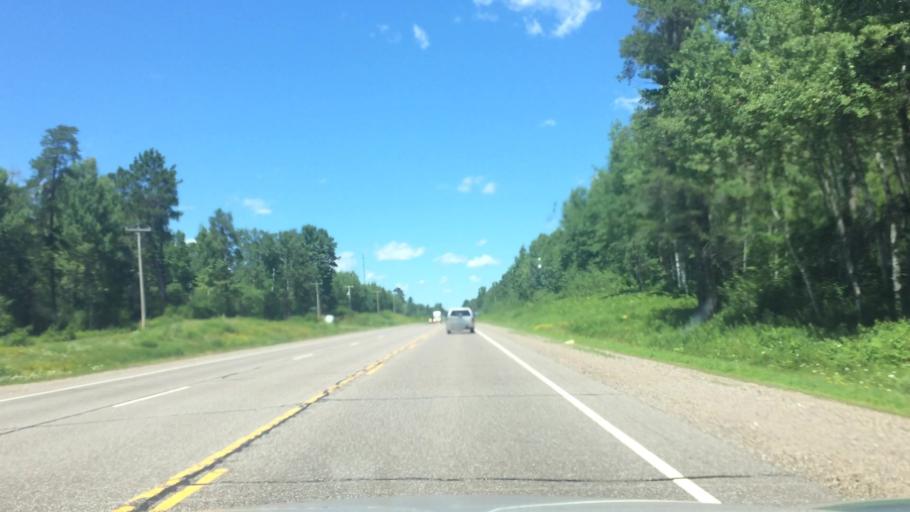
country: US
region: Wisconsin
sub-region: Lincoln County
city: Tomahawk
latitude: 45.6751
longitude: -89.7141
